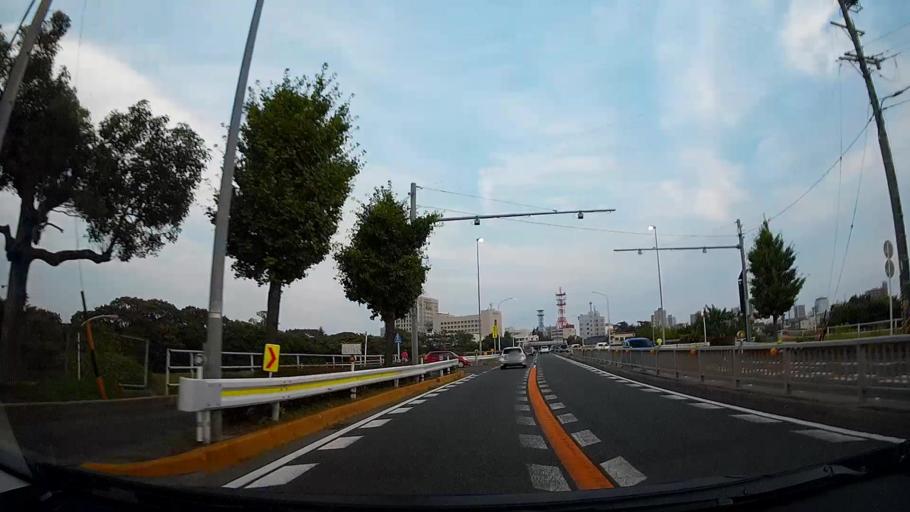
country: JP
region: Aichi
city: Toyohashi
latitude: 34.7734
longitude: 137.3902
